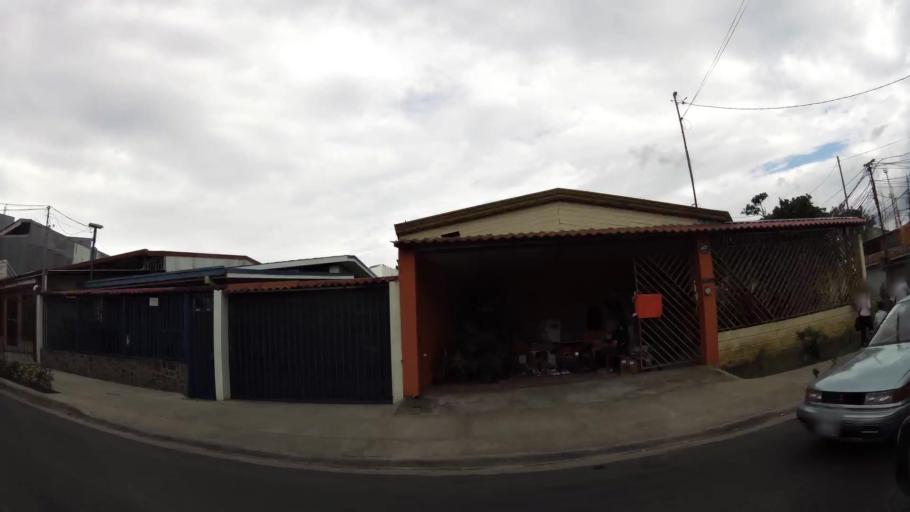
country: CR
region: San Jose
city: Santa Ana
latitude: 9.9547
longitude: -84.1902
